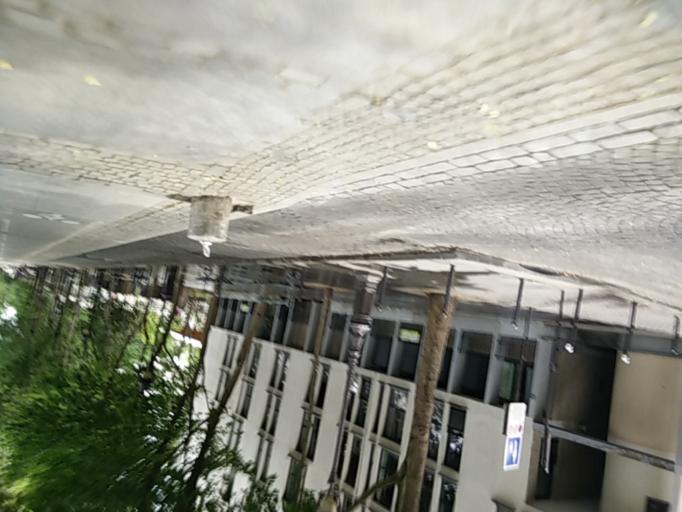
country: FR
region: Ile-de-France
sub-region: Departement de Seine-Saint-Denis
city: Le Pre-Saint-Gervais
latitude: 48.8866
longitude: 2.3771
